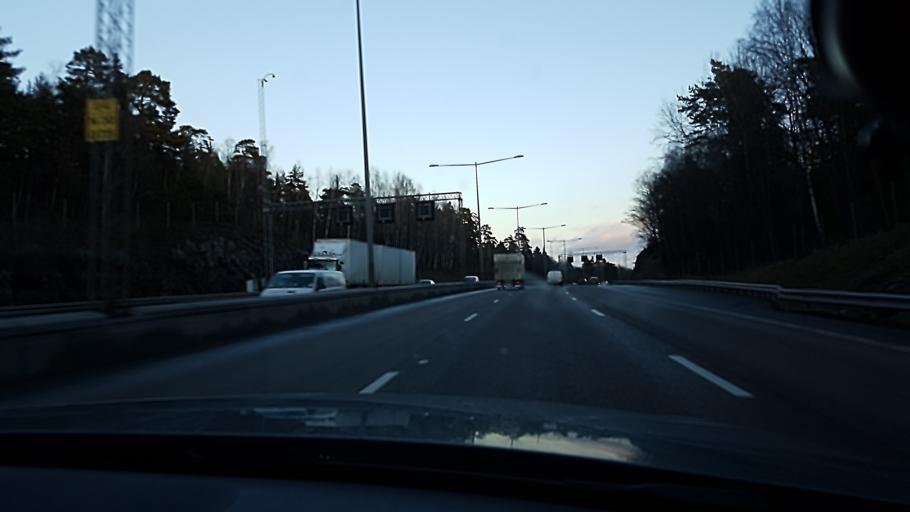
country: SE
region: Stockholm
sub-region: Salems Kommun
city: Ronninge
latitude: 59.2100
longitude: 17.7203
